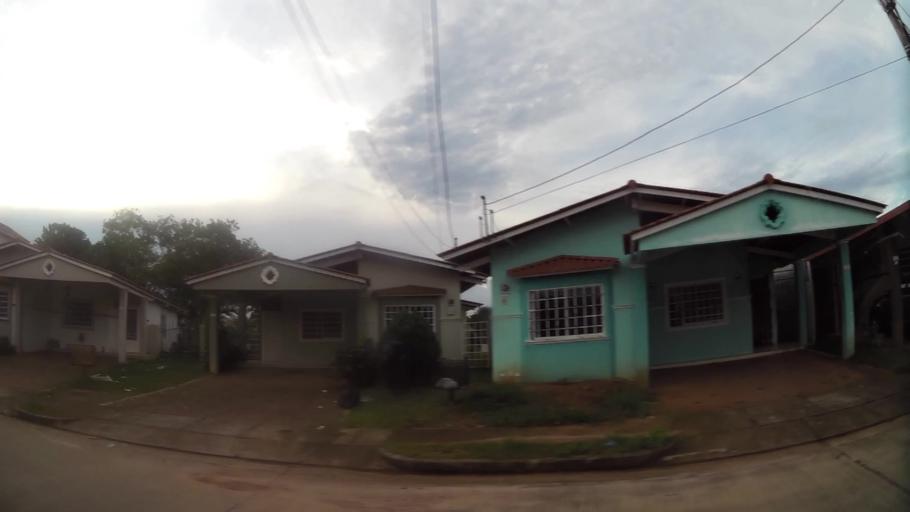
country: PA
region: Panama
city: La Chorrera
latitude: 8.8676
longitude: -79.7670
